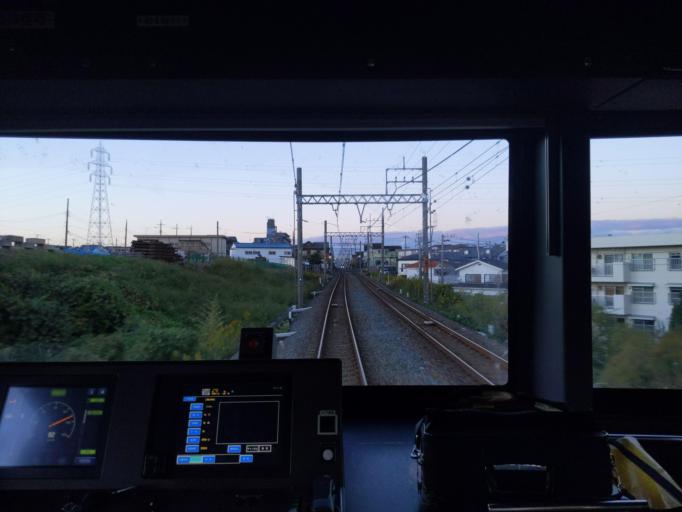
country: JP
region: Chiba
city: Shiroi
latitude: 35.7892
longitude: 139.9990
